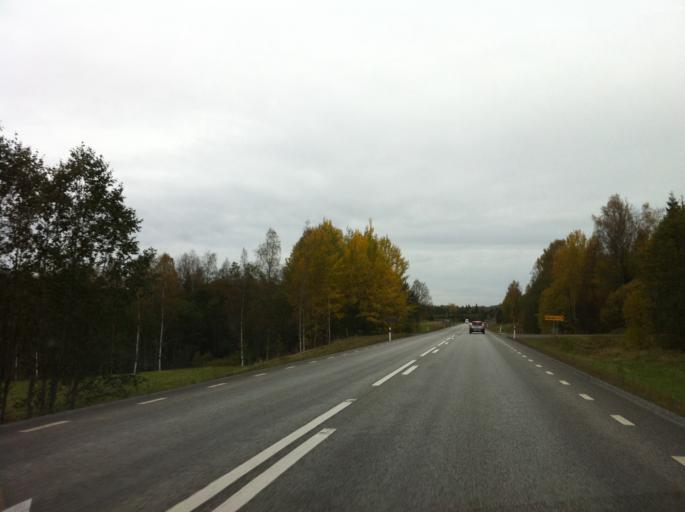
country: SE
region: OErebro
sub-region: Ljusnarsbergs Kommun
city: Kopparberg
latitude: 59.8415
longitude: 15.0813
